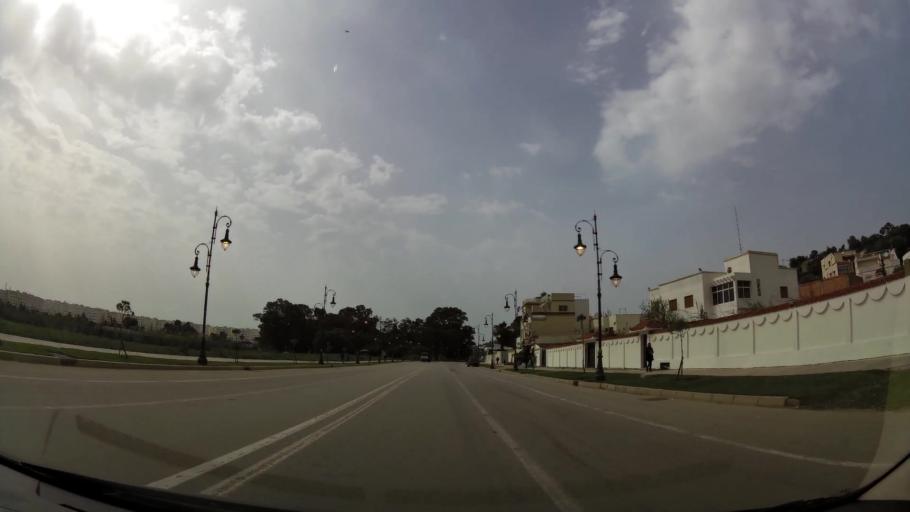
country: MA
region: Tanger-Tetouan
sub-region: Tanger-Assilah
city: Boukhalef
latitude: 35.7408
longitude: -5.8788
